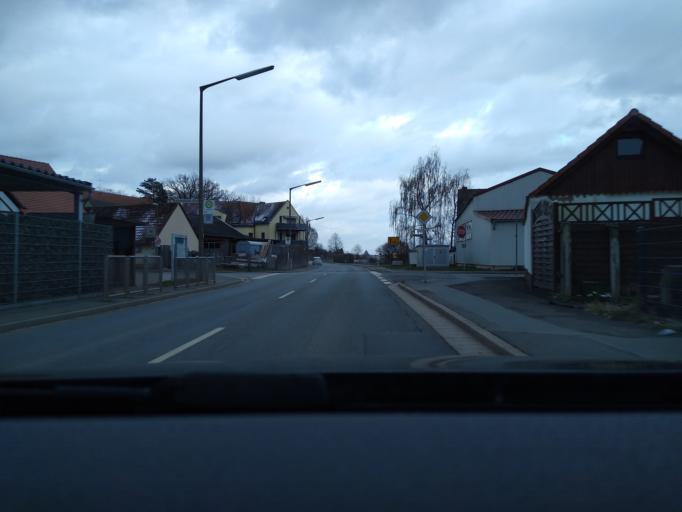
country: DE
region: Bavaria
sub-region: Regierungsbezirk Mittelfranken
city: Zirndorf
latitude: 49.4489
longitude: 10.9255
